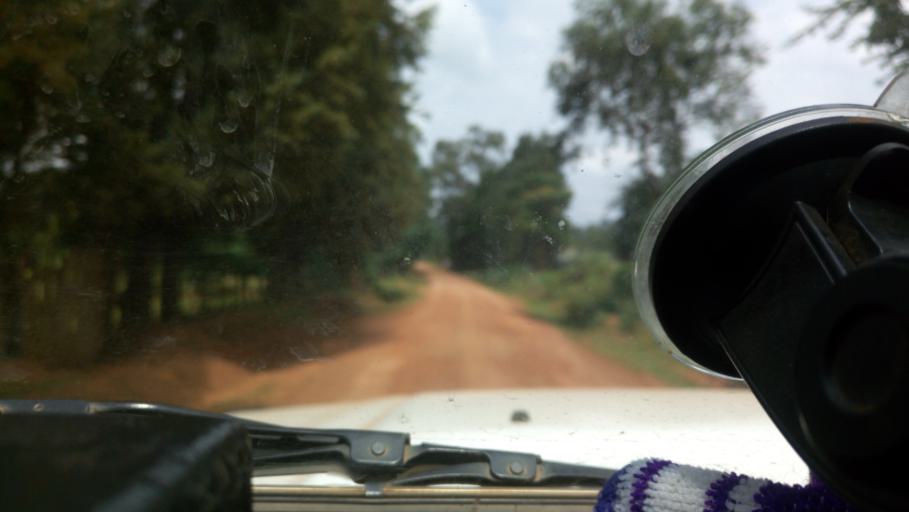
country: KE
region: Kericho
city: Sotik
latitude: -0.6188
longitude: 35.1203
